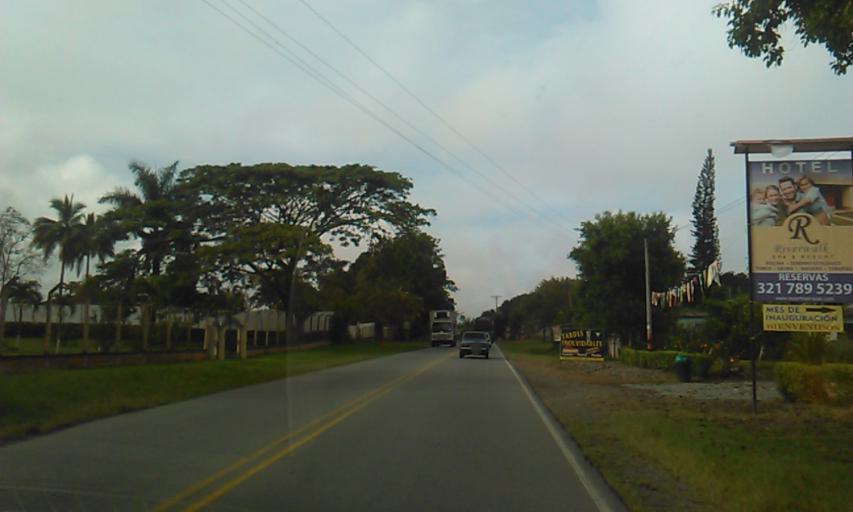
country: CO
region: Quindio
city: Cordoba
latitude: 4.4521
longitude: -75.7141
